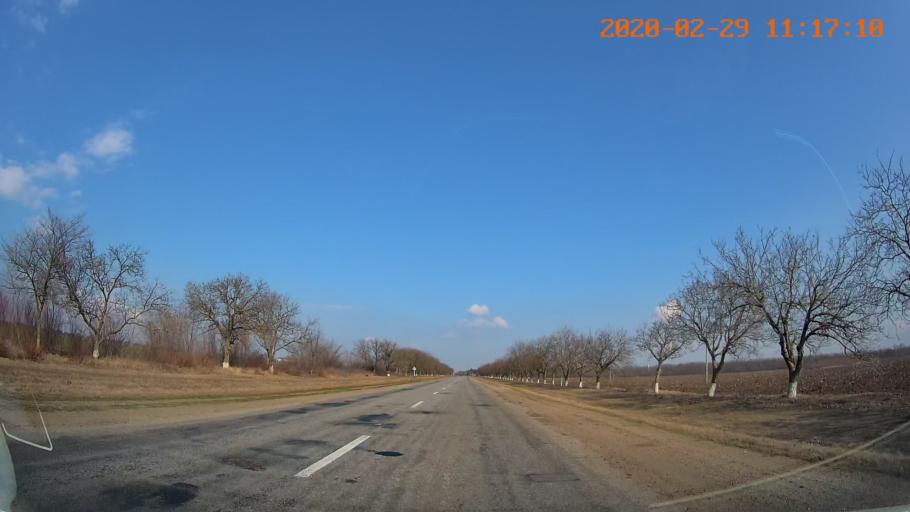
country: MD
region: Telenesti
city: Dubasari
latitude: 47.3185
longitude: 29.1698
